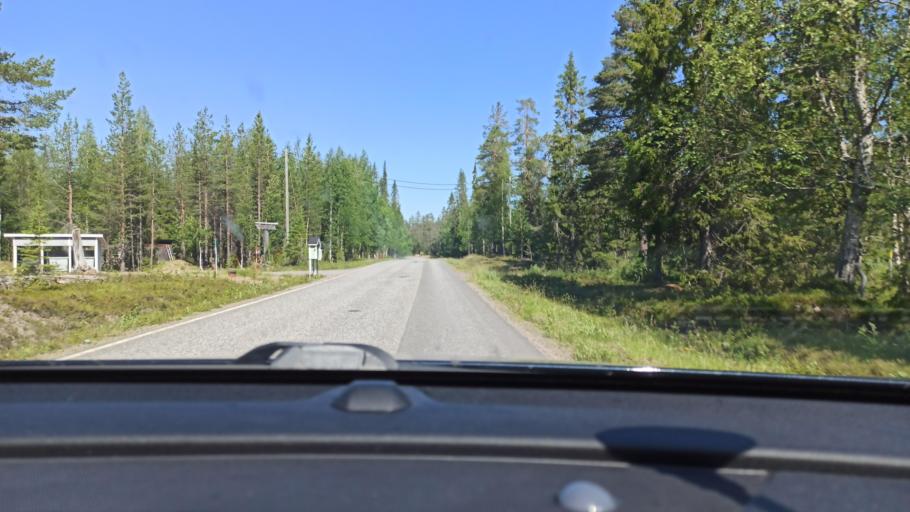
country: FI
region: Lapland
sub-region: Tunturi-Lappi
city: Kolari
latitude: 67.6663
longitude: 24.1606
